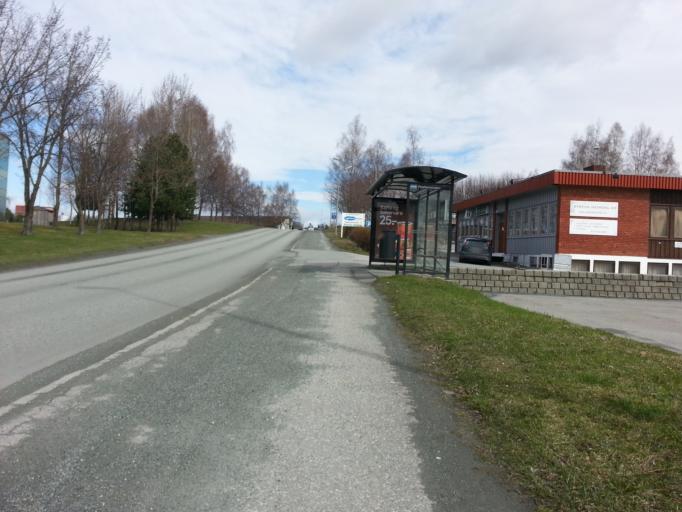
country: NO
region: Sor-Trondelag
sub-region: Trondheim
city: Trondheim
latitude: 63.3971
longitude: 10.3974
